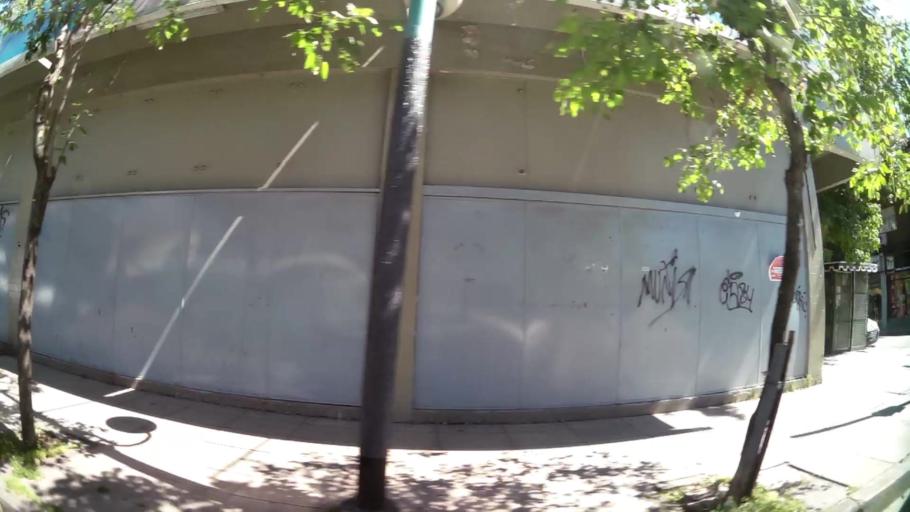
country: AR
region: Buenos Aires
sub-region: Partido de Vicente Lopez
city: Olivos
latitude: -34.5328
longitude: -58.5020
